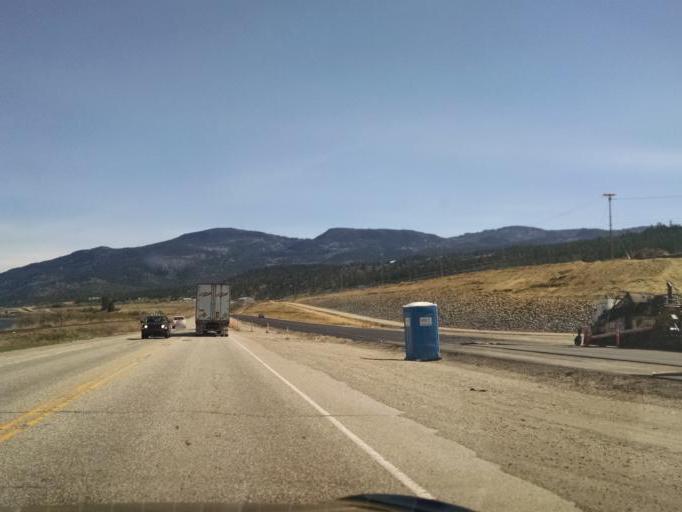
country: CA
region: British Columbia
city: Chase
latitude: 50.6708
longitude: -119.8488
